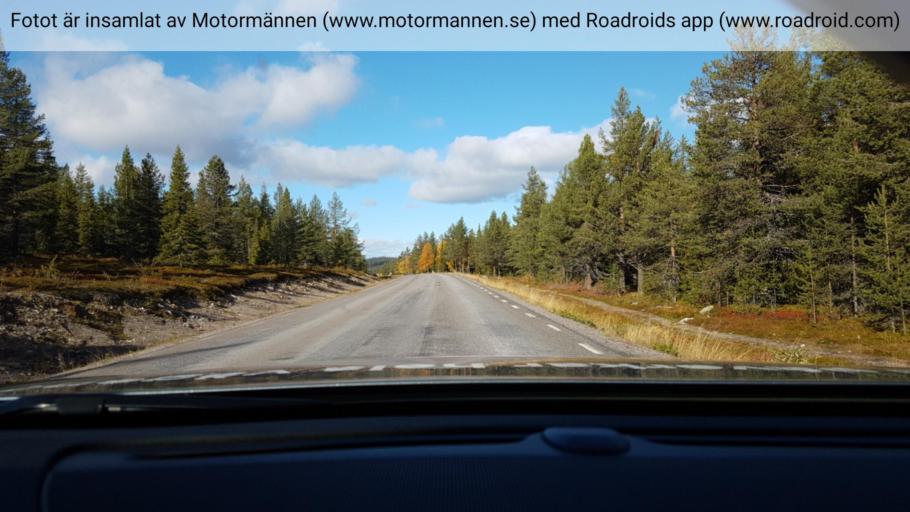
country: SE
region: Norrbotten
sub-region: Arjeplogs Kommun
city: Arjeplog
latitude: 65.9078
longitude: 18.3515
